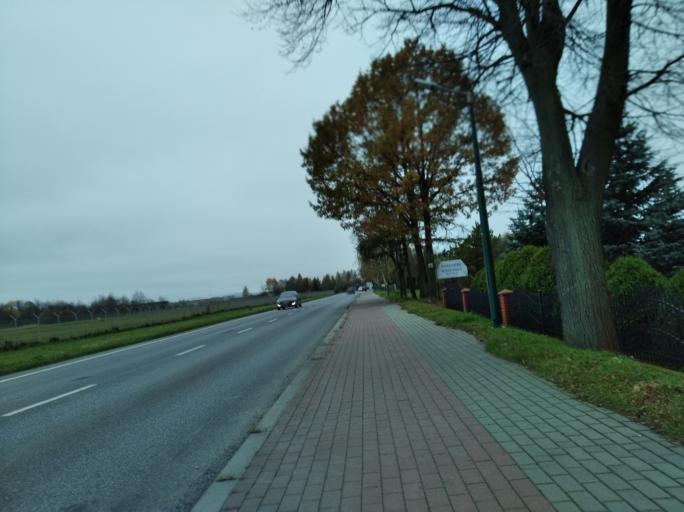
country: PL
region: Subcarpathian Voivodeship
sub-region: Krosno
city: Krosno
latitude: 49.6843
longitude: 21.7235
